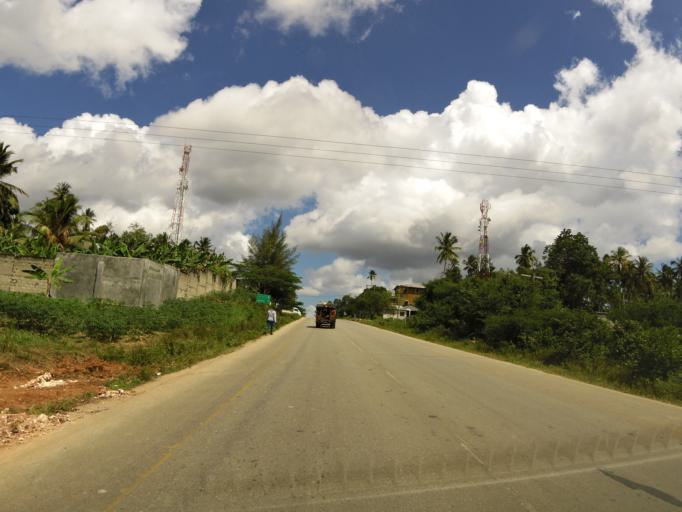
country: TZ
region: Zanzibar Central/South
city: Koani
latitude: -6.1362
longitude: 39.2891
